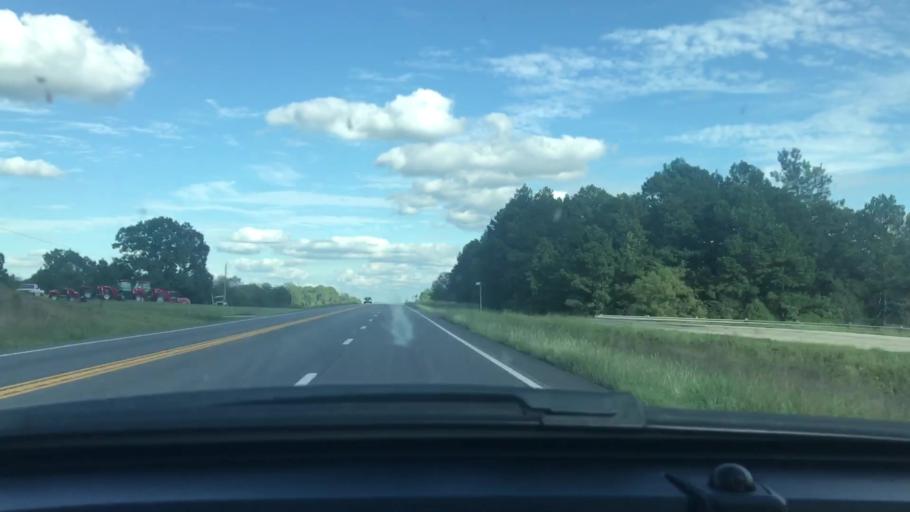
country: US
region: Missouri
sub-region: Oregon County
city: Thayer
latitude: 36.5832
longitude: -91.6126
